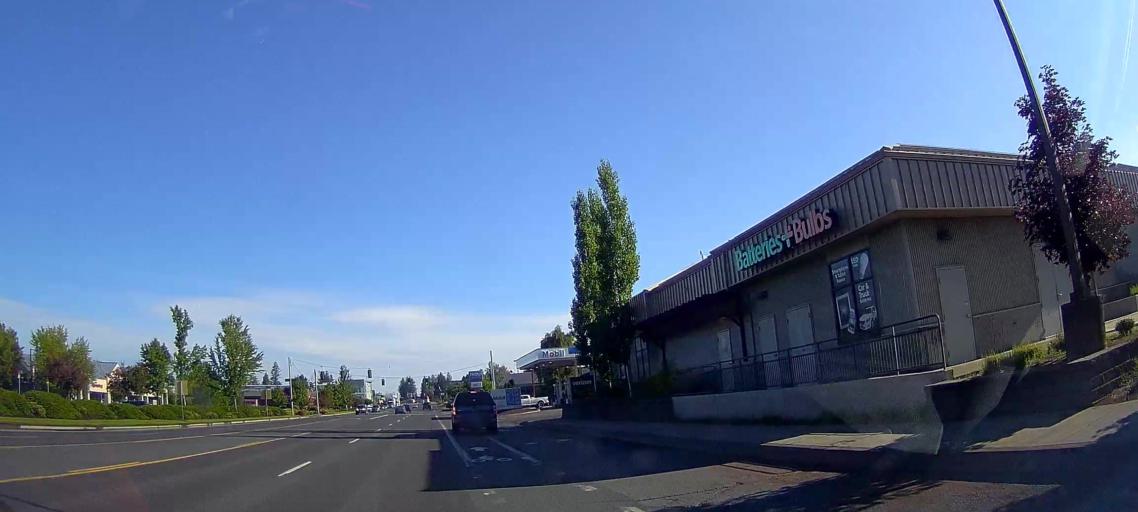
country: US
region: Oregon
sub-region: Deschutes County
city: Bend
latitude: 44.0827
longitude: -121.3053
